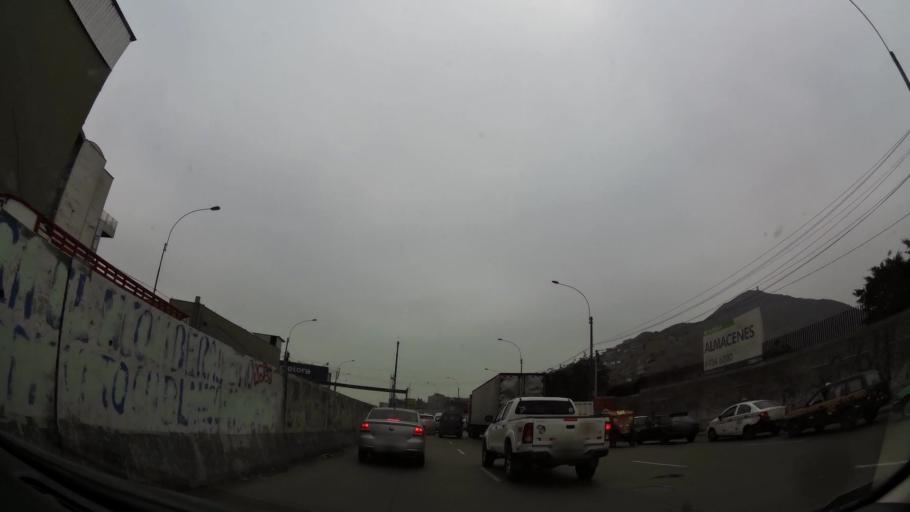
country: PE
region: Lima
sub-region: Lima
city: San Luis
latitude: -12.0604
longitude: -76.9778
